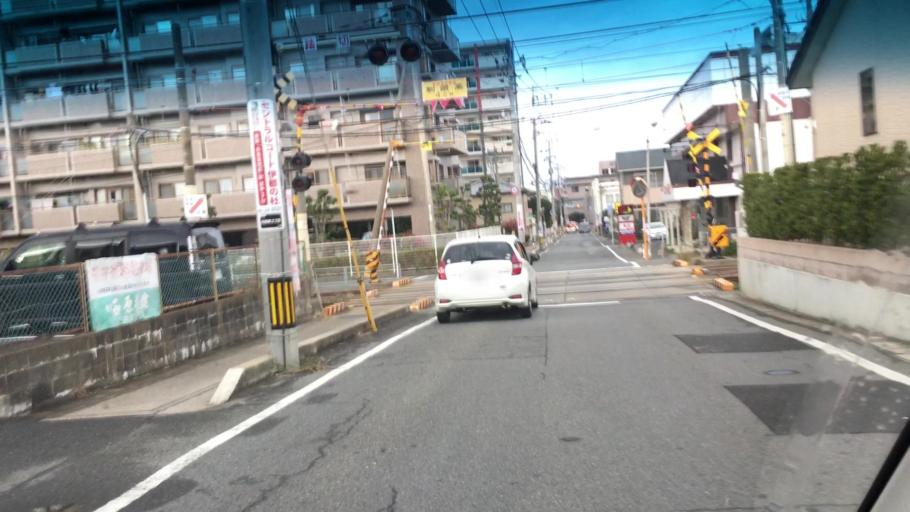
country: JP
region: Fukuoka
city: Maebaru-chuo
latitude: 33.5593
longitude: 130.2098
